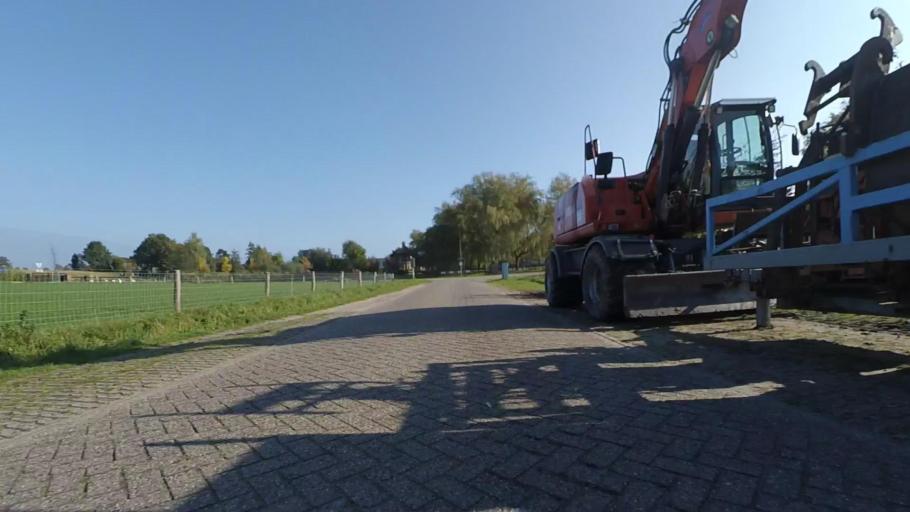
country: NL
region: Gelderland
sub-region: Gemeente Putten
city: Putten
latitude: 52.2508
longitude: 5.5466
